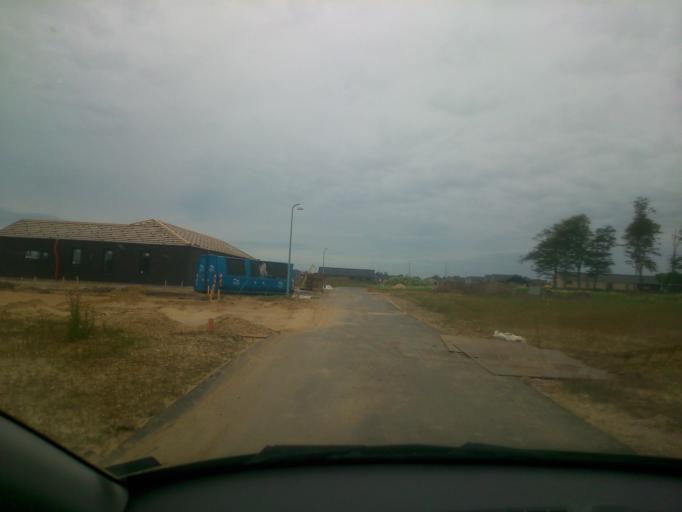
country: DK
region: South Denmark
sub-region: Esbjerg Kommune
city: Esbjerg
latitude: 55.5270
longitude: 8.4339
